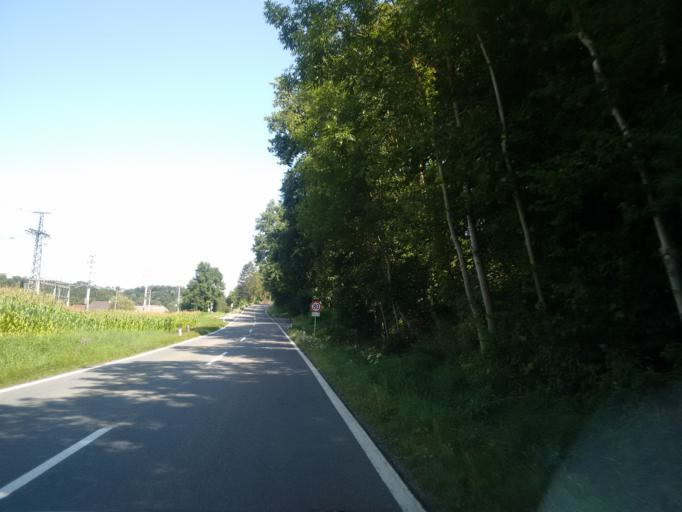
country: AT
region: Upper Austria
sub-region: Politischer Bezirk Kirchdorf an der Krems
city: Kremsmunster
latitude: 48.0241
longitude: 14.1211
